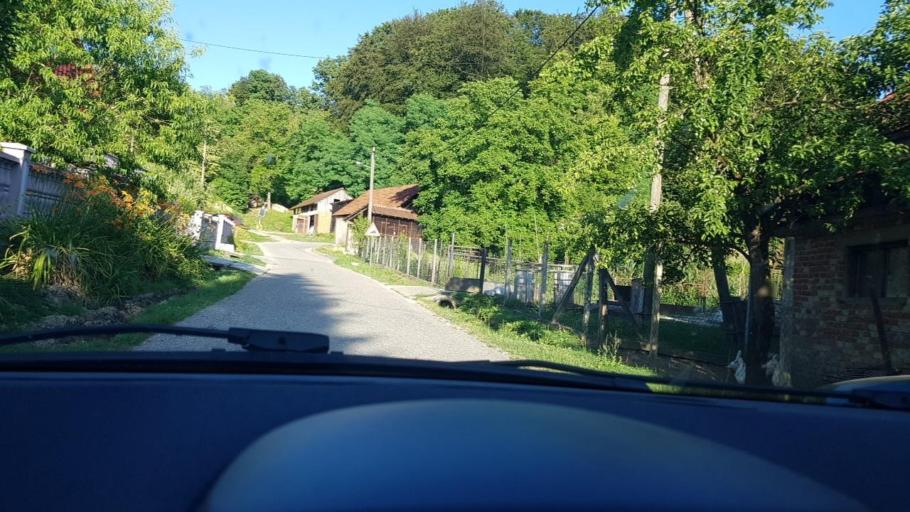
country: HR
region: Krapinsko-Zagorska
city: Mihovljan
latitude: 46.0946
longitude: 15.9453
